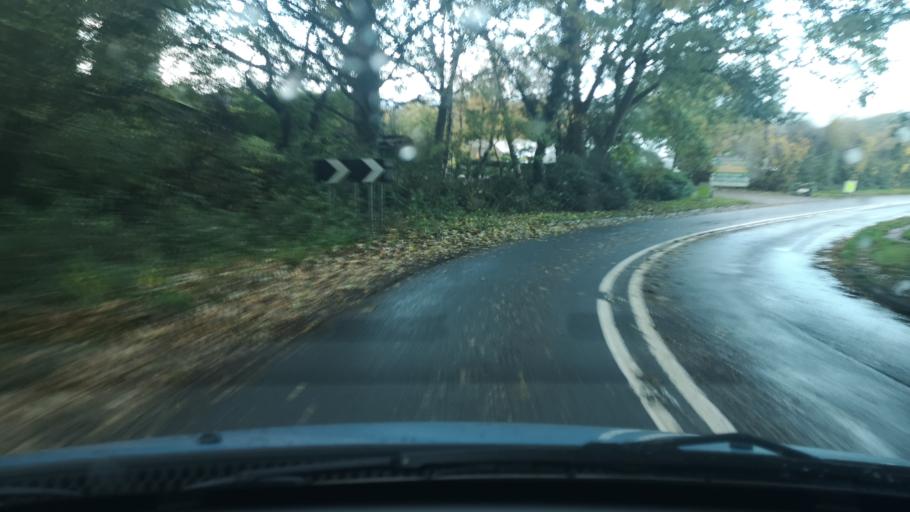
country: GB
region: England
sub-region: City and Borough of Wakefield
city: Woolley
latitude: 53.6250
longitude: -1.5243
